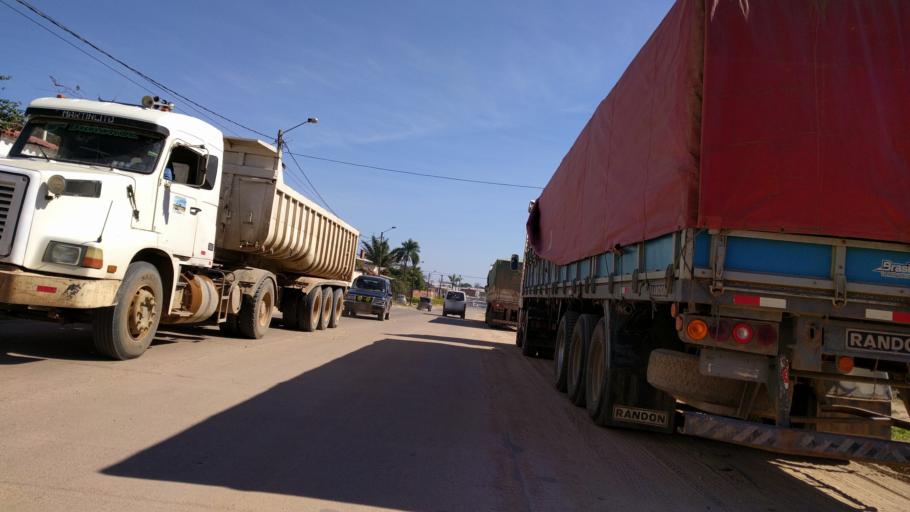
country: BO
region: Santa Cruz
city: Santa Cruz de la Sierra
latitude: -17.8393
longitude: -63.2360
